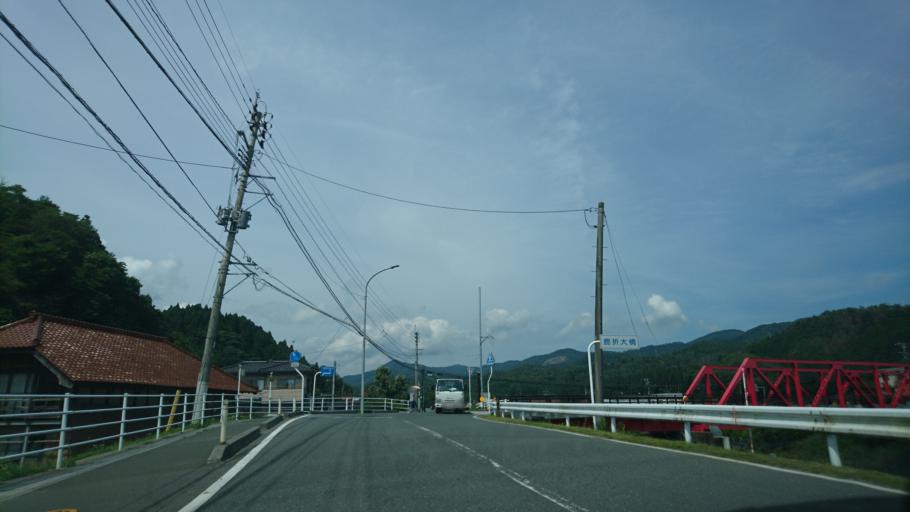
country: JP
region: Iwate
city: Ofunato
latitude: 38.9267
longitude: 141.5827
